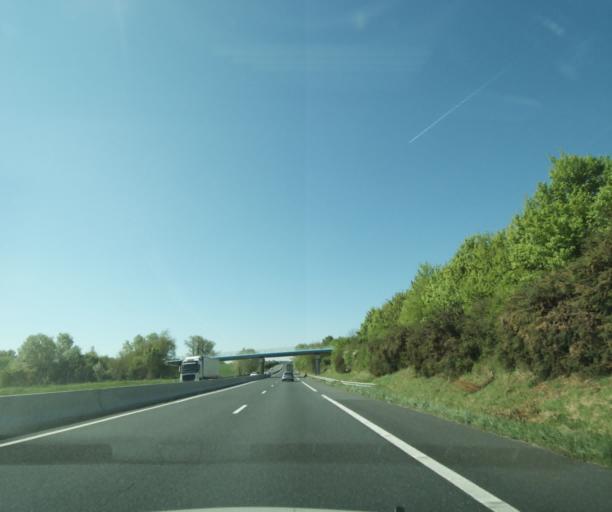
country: FR
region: Centre
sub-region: Departement du Cher
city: Massay
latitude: 47.1662
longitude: 1.9923
